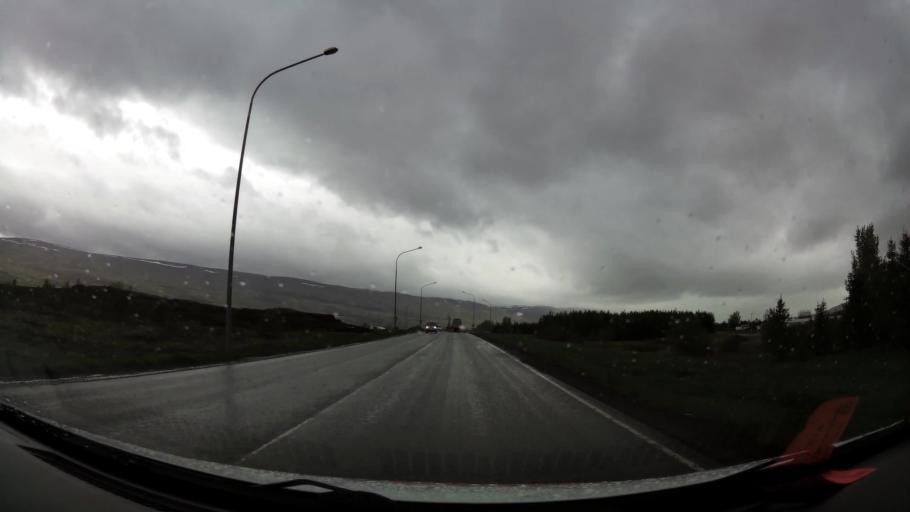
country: IS
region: Northeast
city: Akureyri
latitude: 65.7006
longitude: -18.1446
